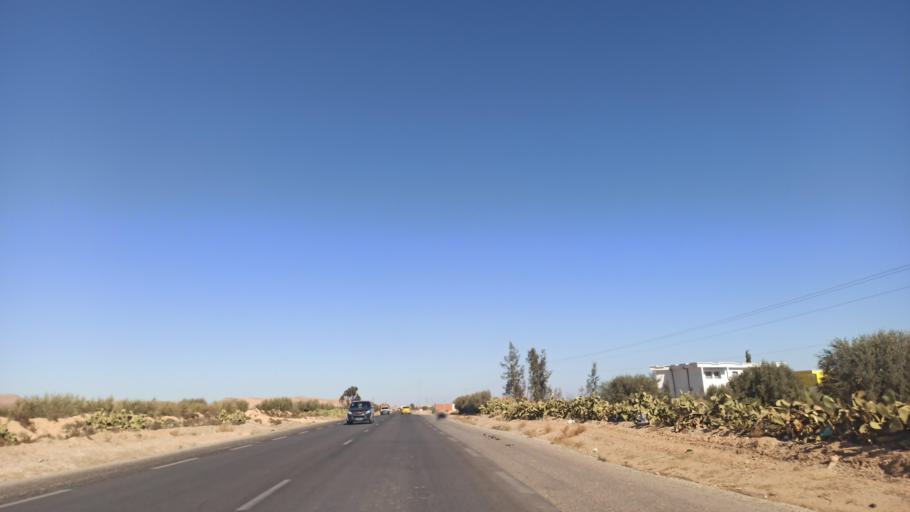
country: TN
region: Sidi Bu Zayd
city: Bi'r al Hufayy
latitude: 34.8988
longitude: 9.1739
